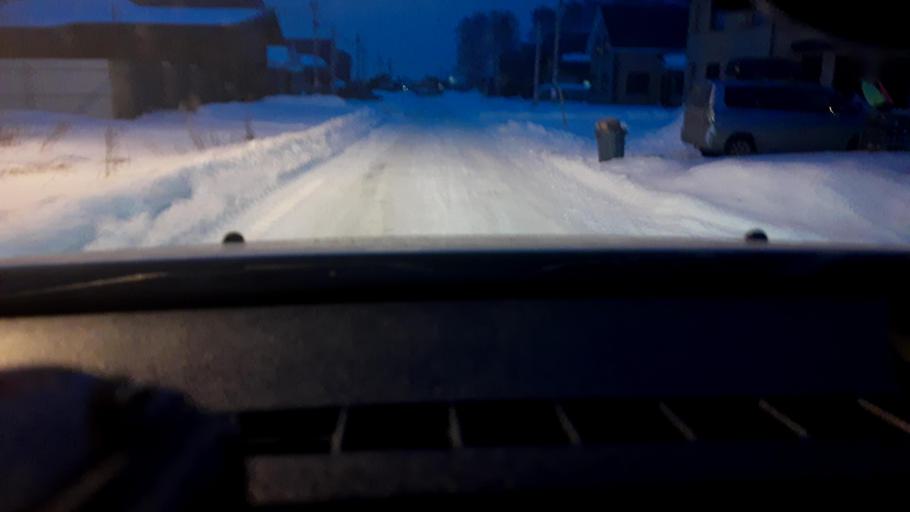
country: RU
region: Bashkortostan
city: Kabakovo
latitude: 54.6091
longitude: 56.1312
